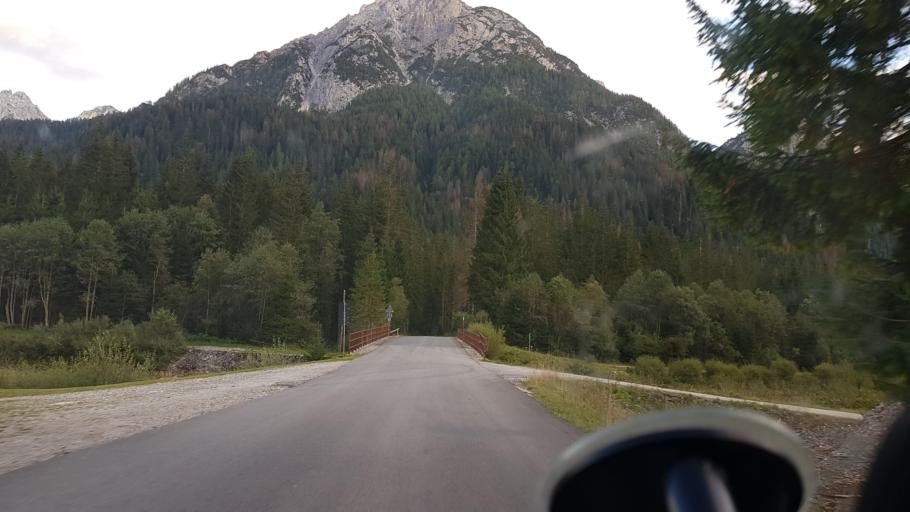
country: IT
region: Veneto
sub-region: Provincia di Belluno
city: San Pietro di Cadore
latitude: 46.6156
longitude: 12.6317
